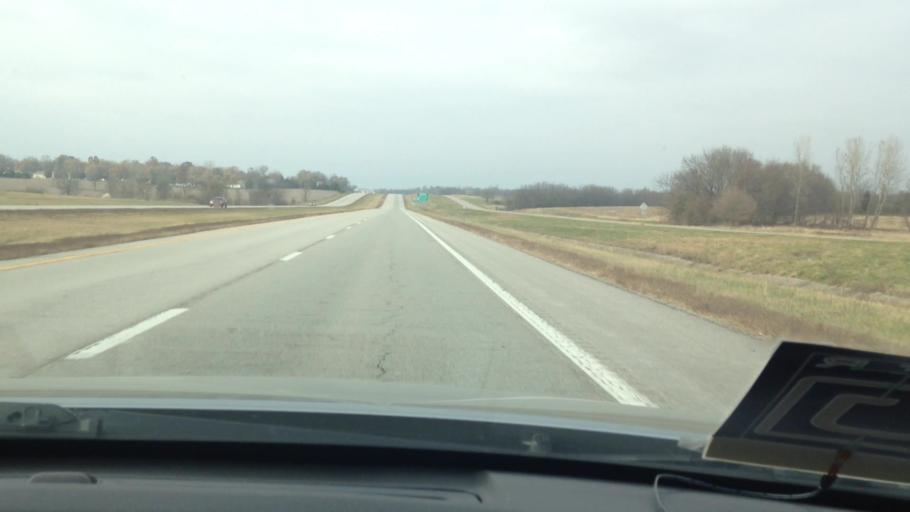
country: US
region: Missouri
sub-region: Cass County
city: Garden City
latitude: 38.5562
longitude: -94.1796
